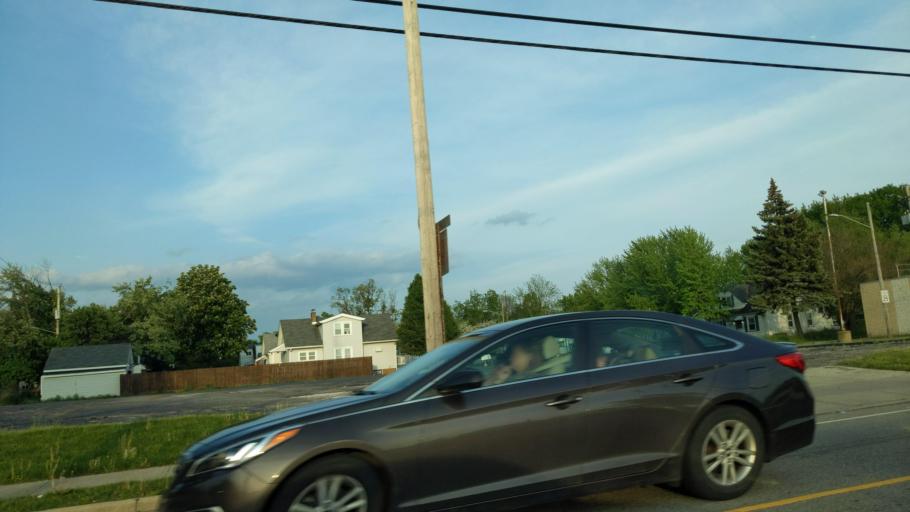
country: US
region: Ohio
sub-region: Cuyahoga County
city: Brook Park
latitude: 41.4263
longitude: -81.7802
